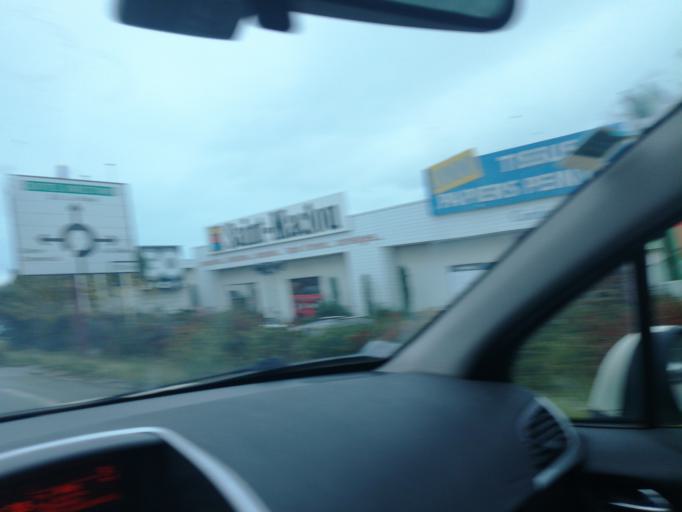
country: FR
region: Provence-Alpes-Cote d'Azur
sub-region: Departement du Var
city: Puget-sur-Argens
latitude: 43.4451
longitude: 6.6996
